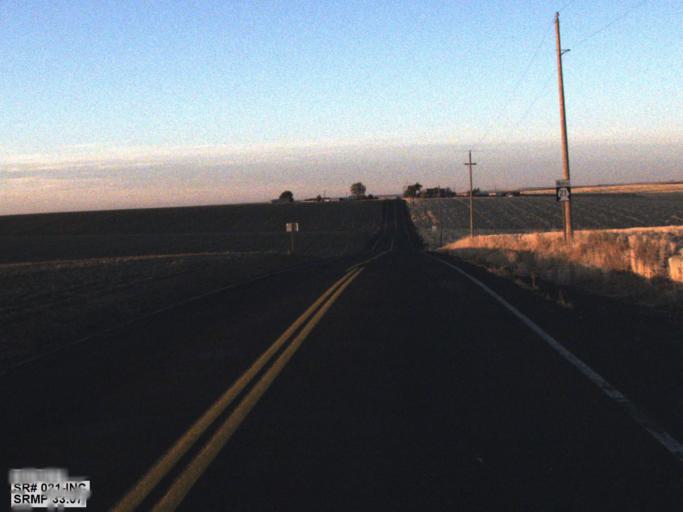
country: US
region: Washington
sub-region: Adams County
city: Ritzville
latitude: 47.0293
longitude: -118.6633
